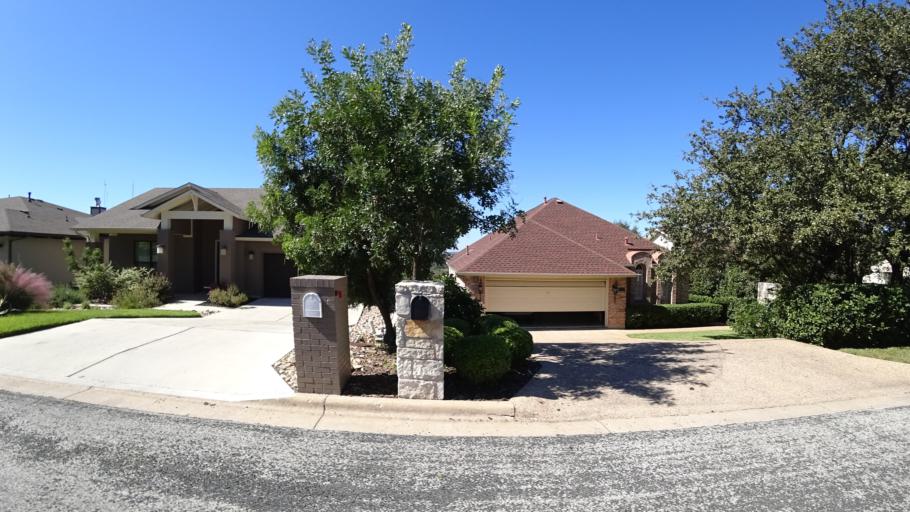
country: US
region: Texas
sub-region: Travis County
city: West Lake Hills
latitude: 30.3449
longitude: -97.7845
